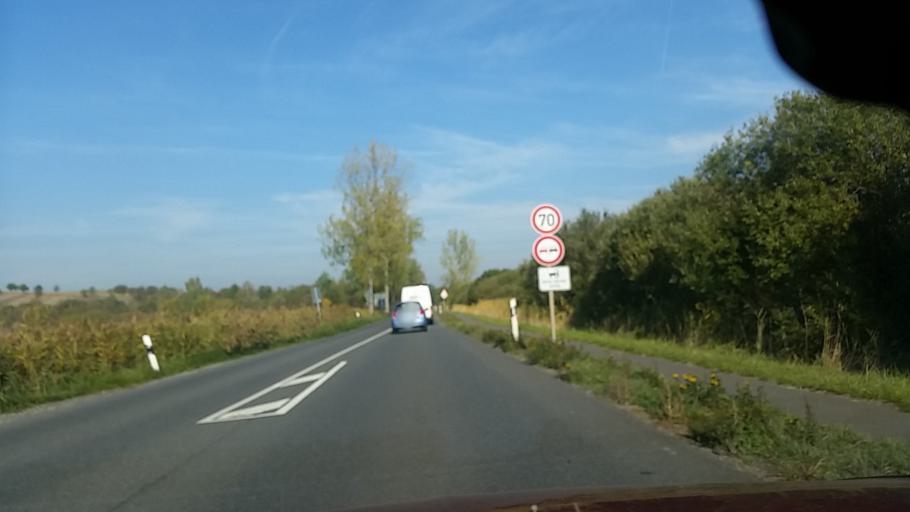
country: DE
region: Lower Saxony
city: Weyhausen
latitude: 52.4366
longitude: 10.7146
